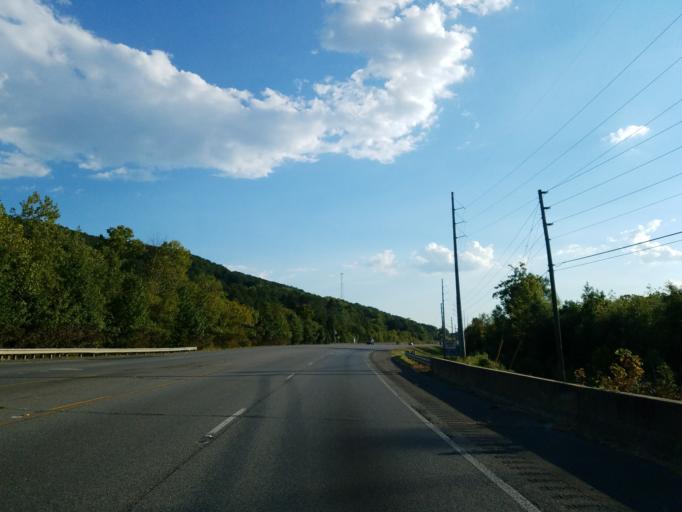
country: US
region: Georgia
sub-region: Murray County
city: Chatsworth
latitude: 34.8119
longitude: -84.7661
